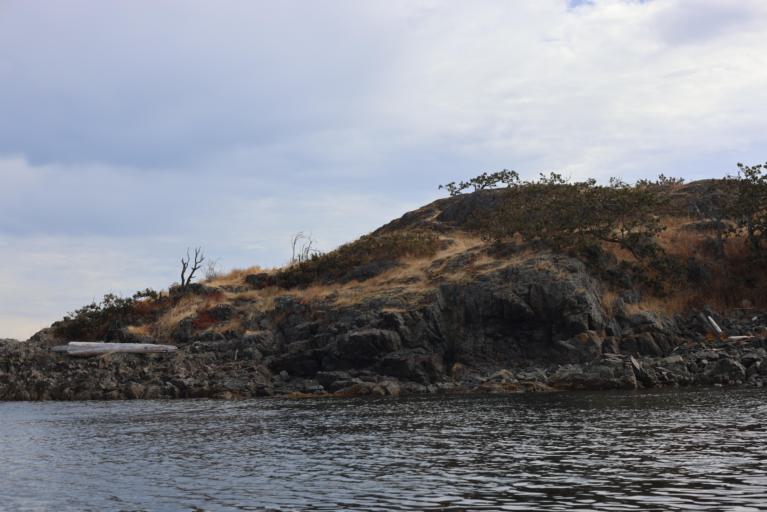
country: CA
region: British Columbia
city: Nanaimo
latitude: 49.2289
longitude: -123.9563
